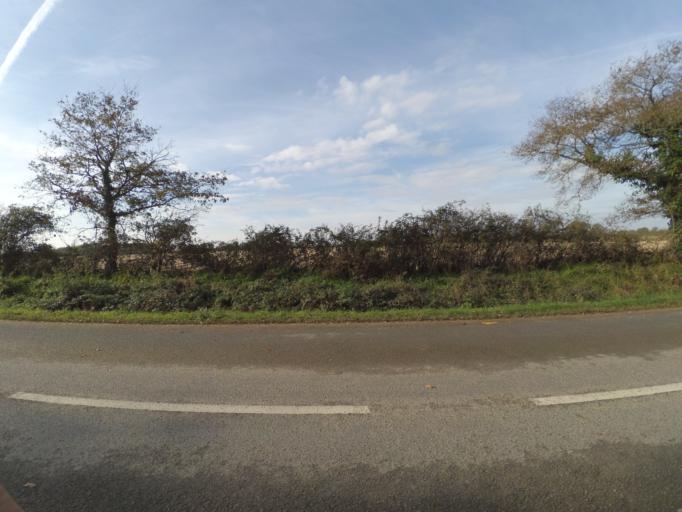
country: FR
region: Pays de la Loire
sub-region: Departement de la Vendee
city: Saint-Hilaire-de-Loulay
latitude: 47.0056
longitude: -1.3677
